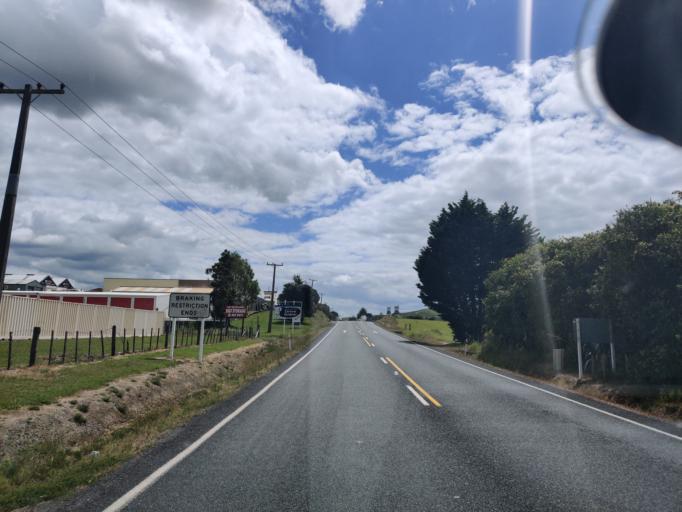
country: NZ
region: Northland
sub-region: Far North District
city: Paihia
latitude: -35.2808
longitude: 174.0488
